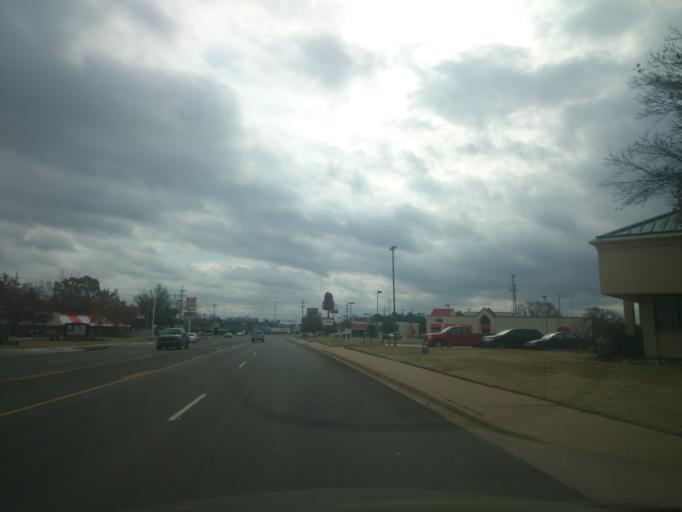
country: US
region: Oklahoma
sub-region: Payne County
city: Stillwater
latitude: 36.1336
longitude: -97.0621
